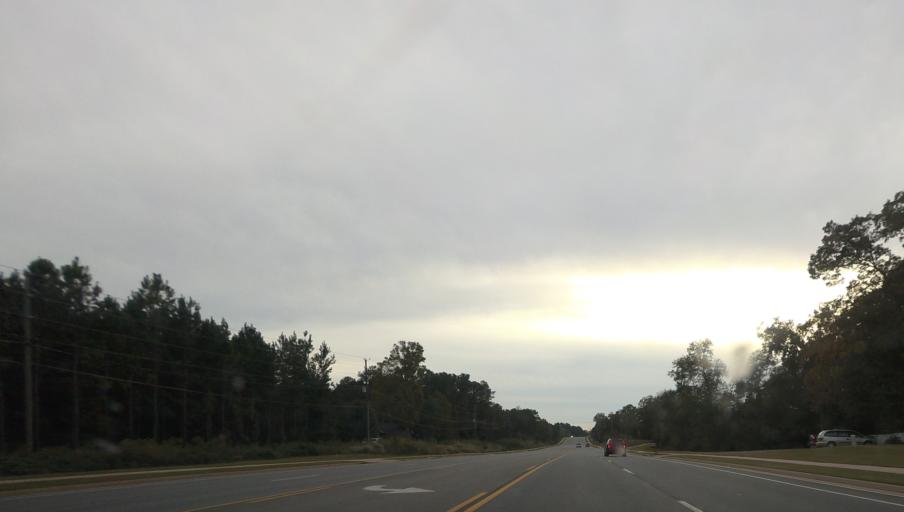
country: US
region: Georgia
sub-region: Houston County
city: Perry
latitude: 32.4881
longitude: -83.6871
